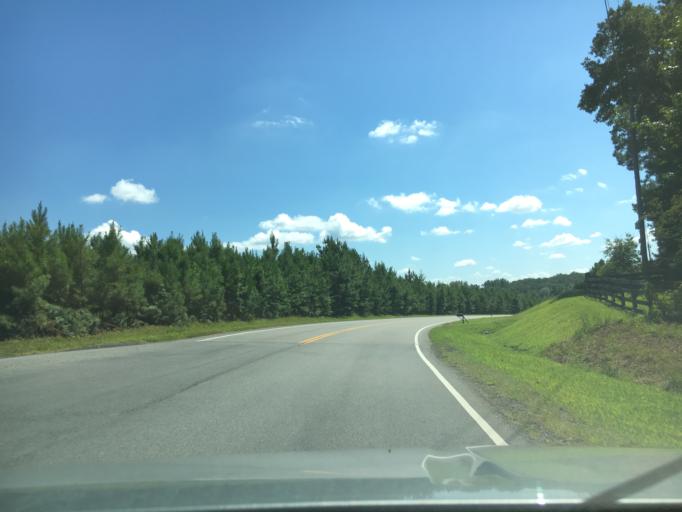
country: US
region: Virginia
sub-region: Amelia County
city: Amelia Court House
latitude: 37.4086
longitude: -77.8933
